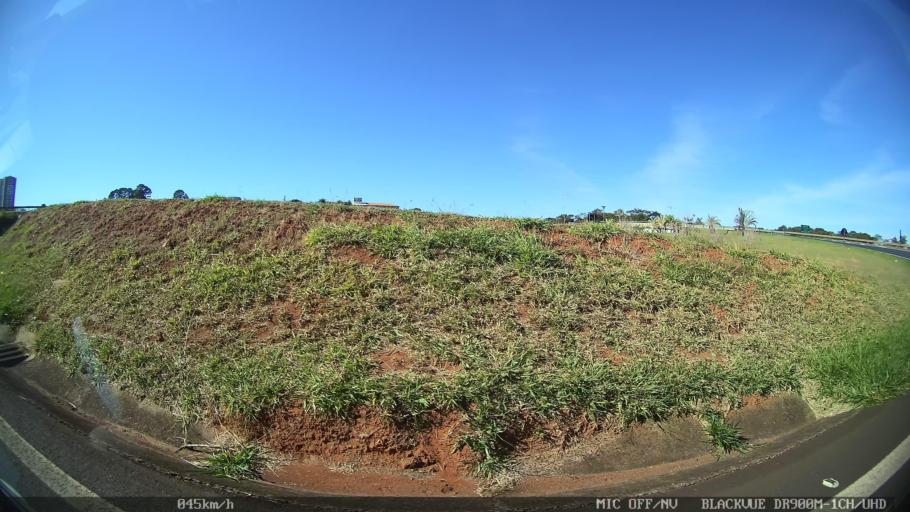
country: BR
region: Sao Paulo
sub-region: Franca
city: Franca
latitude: -20.5608
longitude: -47.4136
